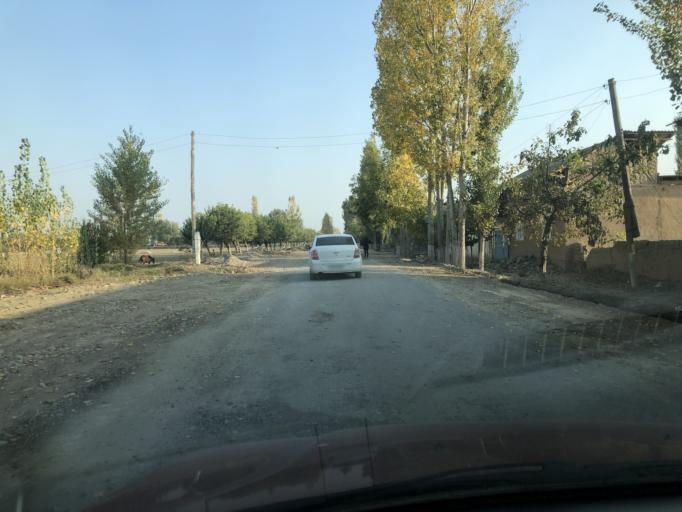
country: UZ
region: Namangan
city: Uychi
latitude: 41.0657
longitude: 71.9861
